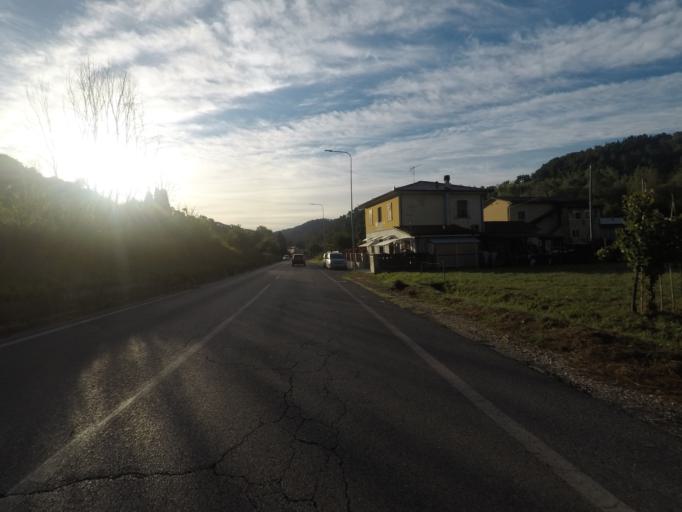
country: IT
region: Tuscany
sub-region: Provincia di Lucca
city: Stiava
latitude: 43.9094
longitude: 10.3415
